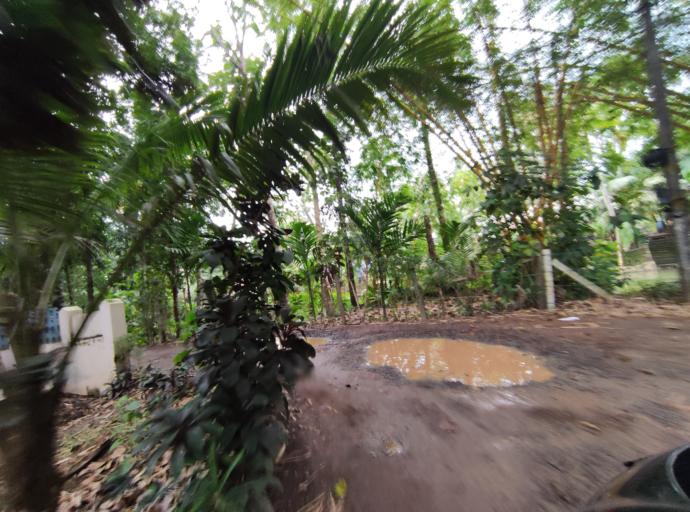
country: IN
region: Kerala
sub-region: Kottayam
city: Kottayam
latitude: 9.5921
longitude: 76.4897
